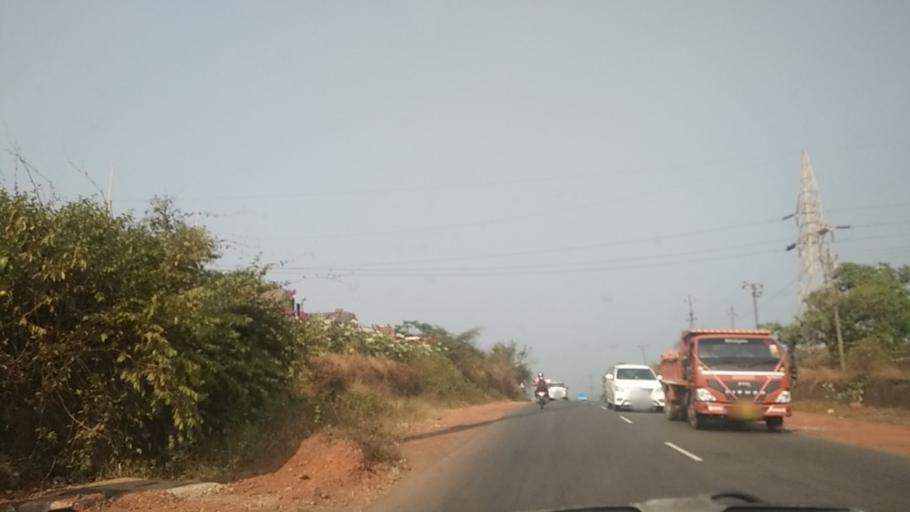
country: IN
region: Goa
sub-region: North Goa
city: Colovale
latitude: 15.6361
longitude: 73.8305
